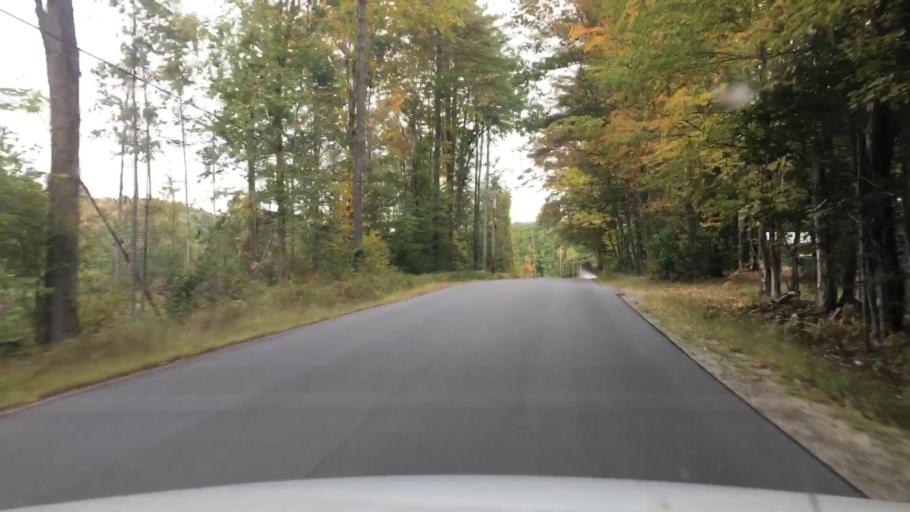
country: US
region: Maine
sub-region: Cumberland County
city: Harrison
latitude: 44.2490
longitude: -70.7215
